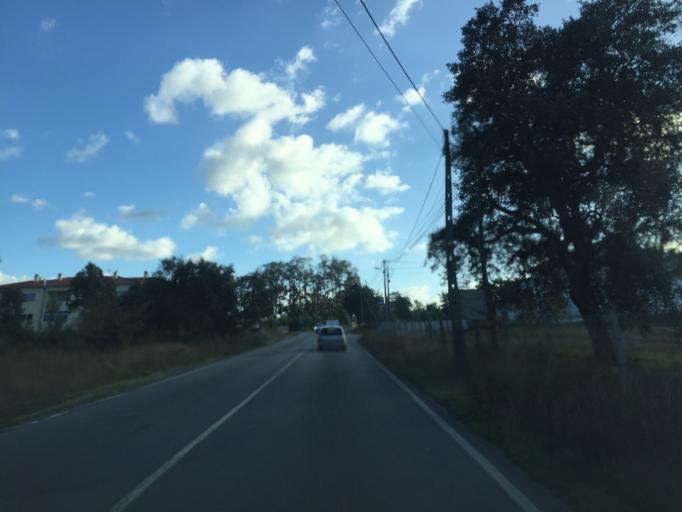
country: PT
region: Leiria
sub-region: Leiria
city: Souto da Carpalhosa
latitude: 39.8571
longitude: -8.8353
